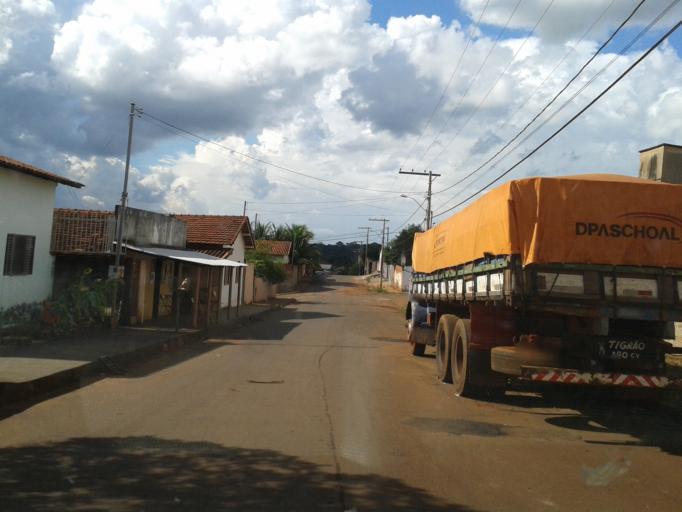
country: BR
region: Minas Gerais
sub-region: Capinopolis
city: Capinopolis
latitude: -18.6851
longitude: -49.5785
